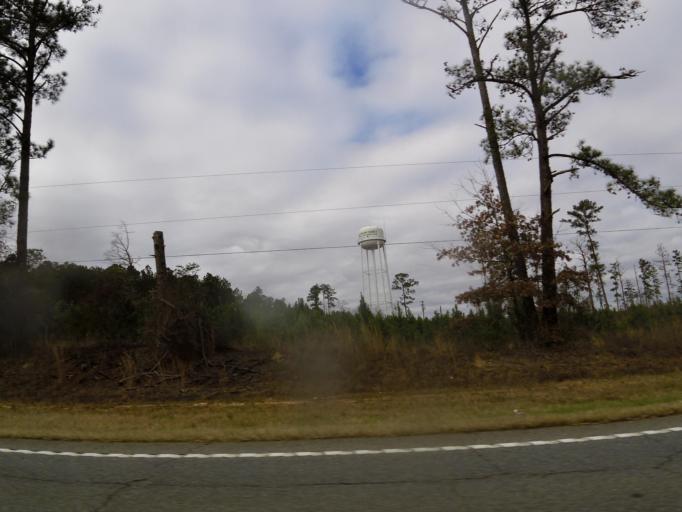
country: US
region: Georgia
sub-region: Quitman County
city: Georgetown
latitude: 31.8603
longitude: -85.0313
